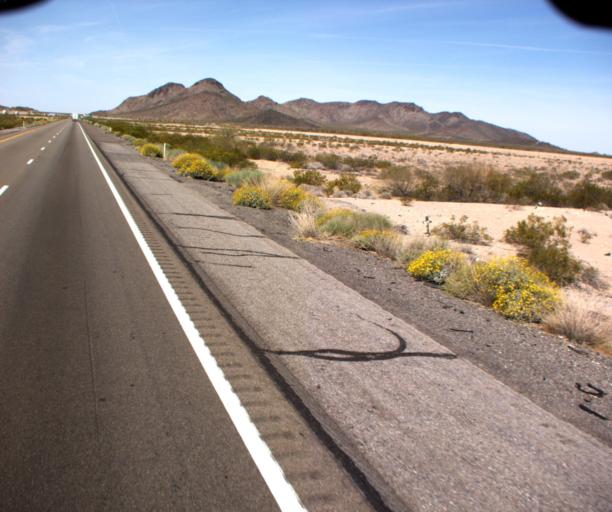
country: US
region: Arizona
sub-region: La Paz County
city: Salome
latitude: 33.6073
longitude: -113.6063
